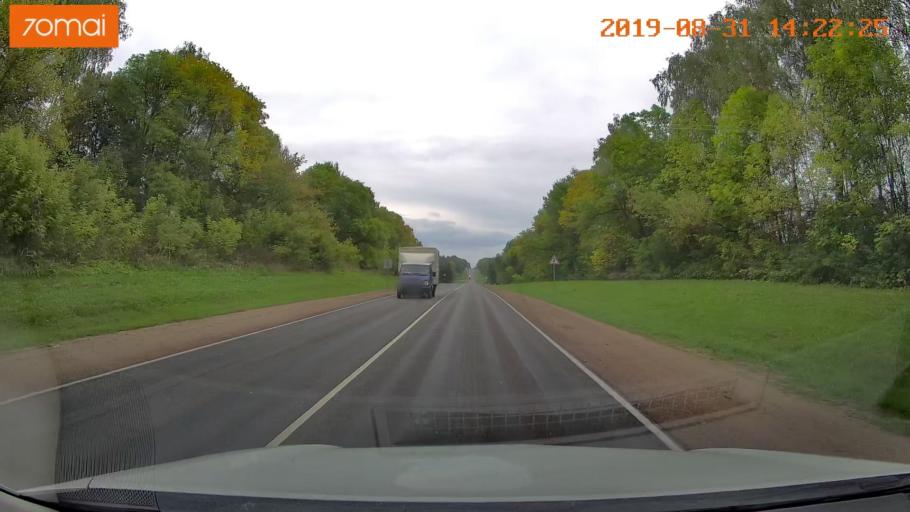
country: RU
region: Smolensk
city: Yekimovichi
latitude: 54.0917
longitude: 33.2181
